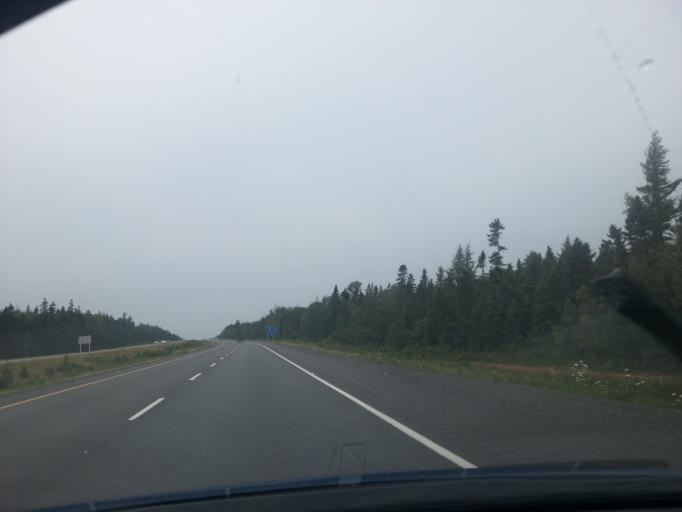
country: CA
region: Nova Scotia
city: Truro
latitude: 45.3977
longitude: -63.4642
